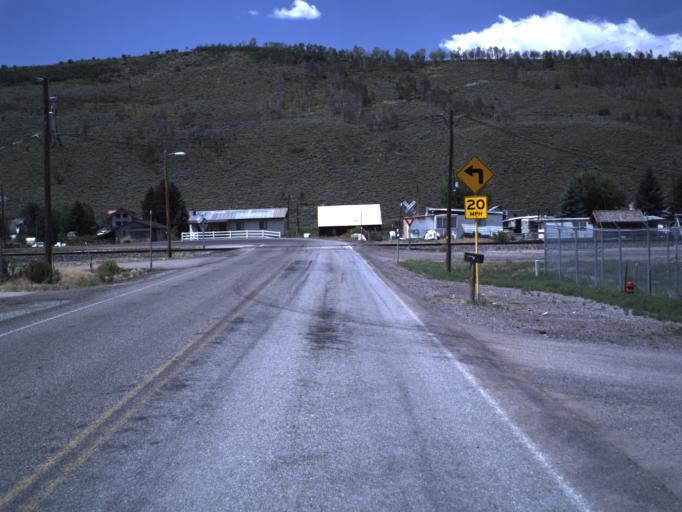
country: US
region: Utah
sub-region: Sanpete County
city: Fairview
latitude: 39.7287
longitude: -111.1587
